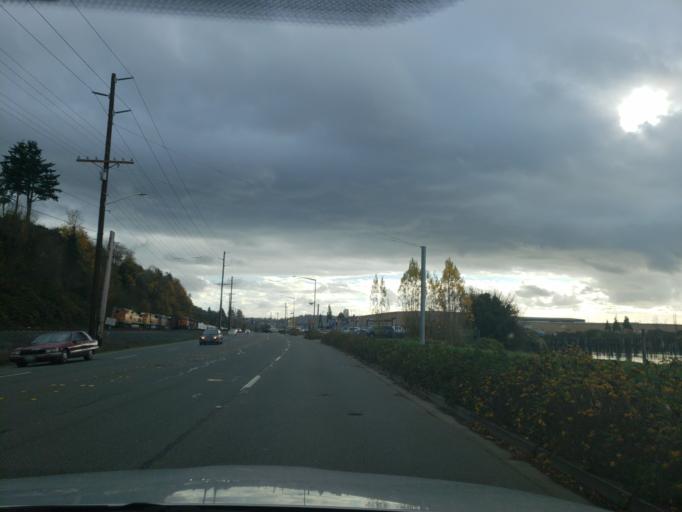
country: US
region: Washington
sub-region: Snohomish County
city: Everett
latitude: 48.0064
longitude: -122.2143
